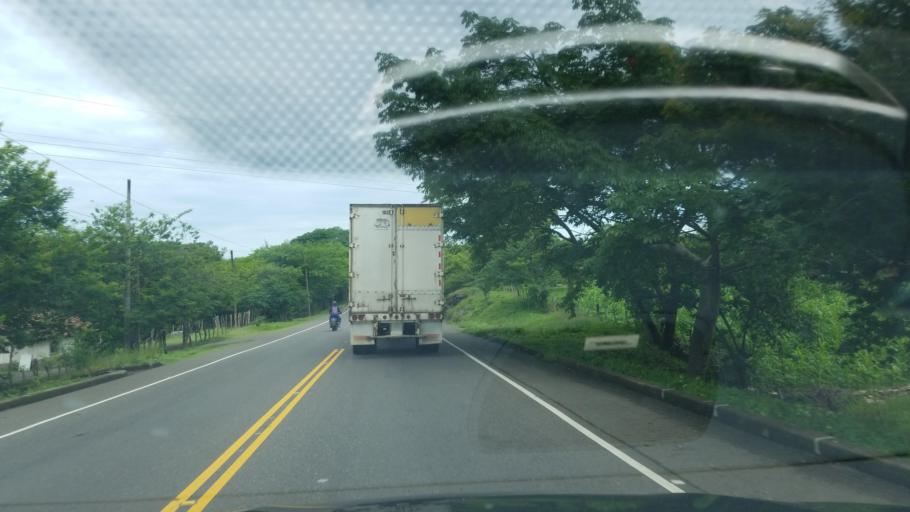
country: HN
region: Valle
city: Goascoran
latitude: 13.5397
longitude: -87.6126
